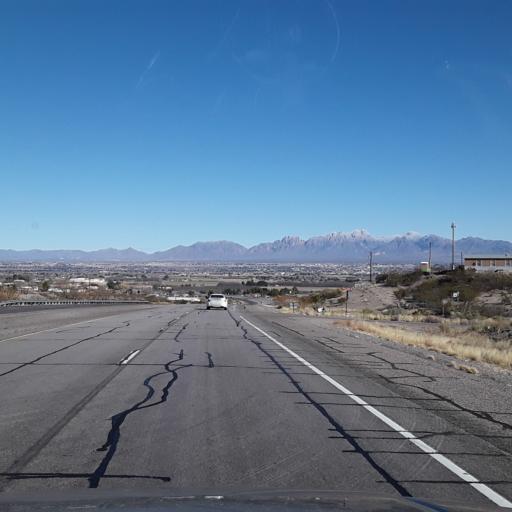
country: US
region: New Mexico
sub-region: Dona Ana County
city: Mesilla
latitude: 32.2916
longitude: -106.8678
